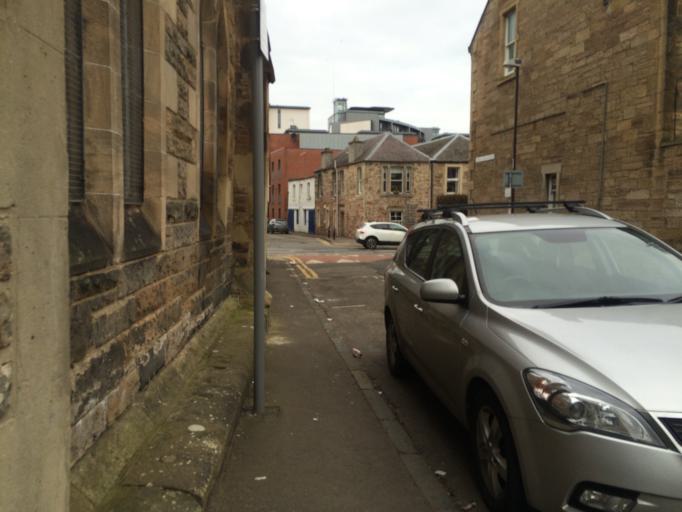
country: GB
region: Scotland
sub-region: Edinburgh
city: Edinburgh
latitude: 55.9410
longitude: -3.2083
